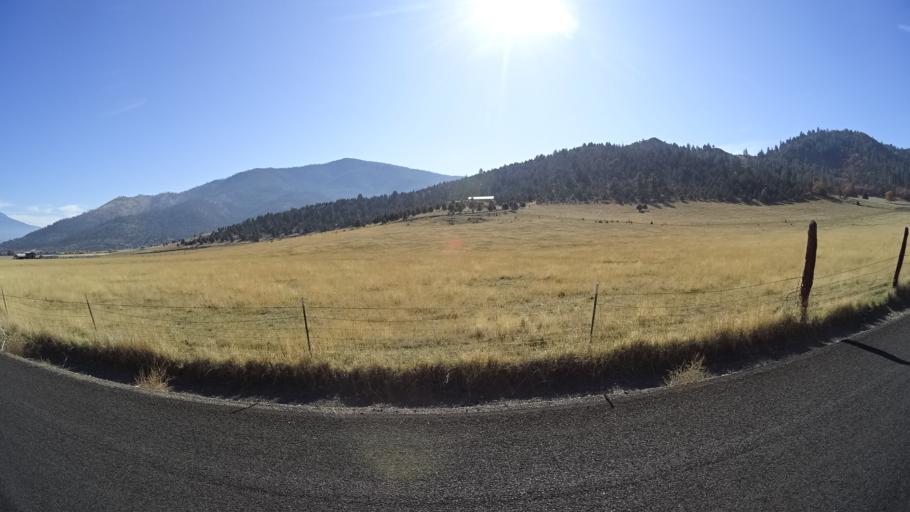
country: US
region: California
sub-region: Siskiyou County
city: Weed
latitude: 41.5030
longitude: -122.5602
